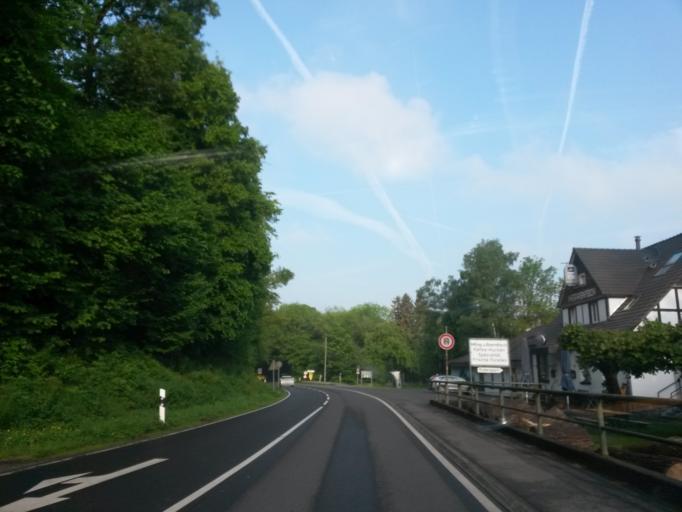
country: DE
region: North Rhine-Westphalia
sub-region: Regierungsbezirk Koln
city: Much
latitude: 50.8843
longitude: 7.3881
